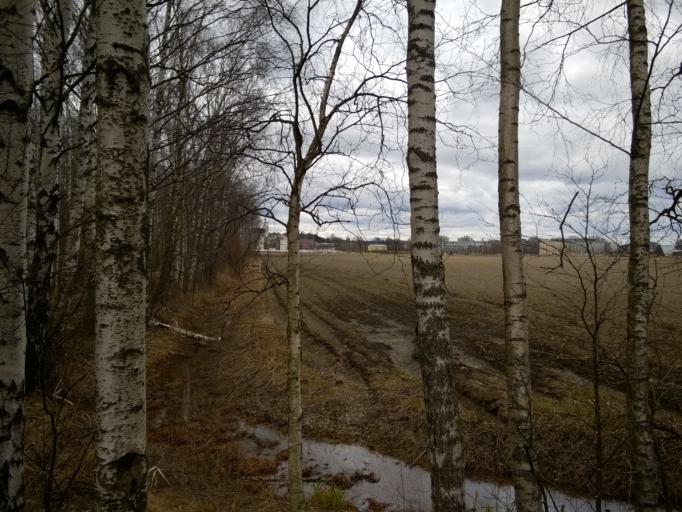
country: FI
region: Uusimaa
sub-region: Helsinki
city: Vantaa
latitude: 60.2212
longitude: 25.0021
